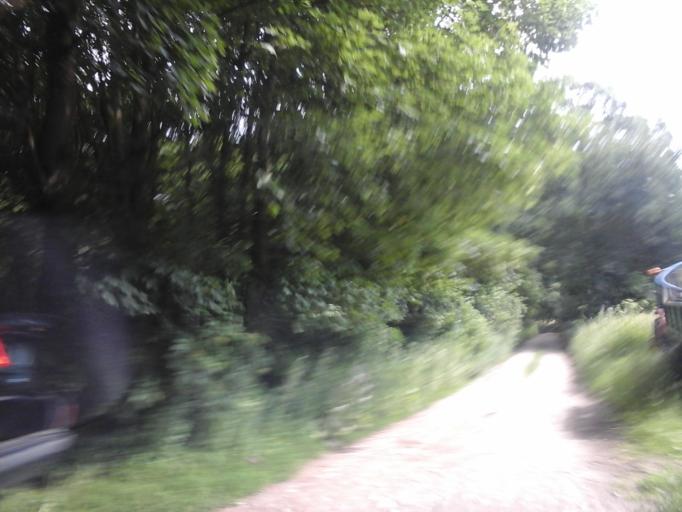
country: PL
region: West Pomeranian Voivodeship
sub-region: Powiat choszczenski
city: Recz
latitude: 53.2815
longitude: 15.6283
